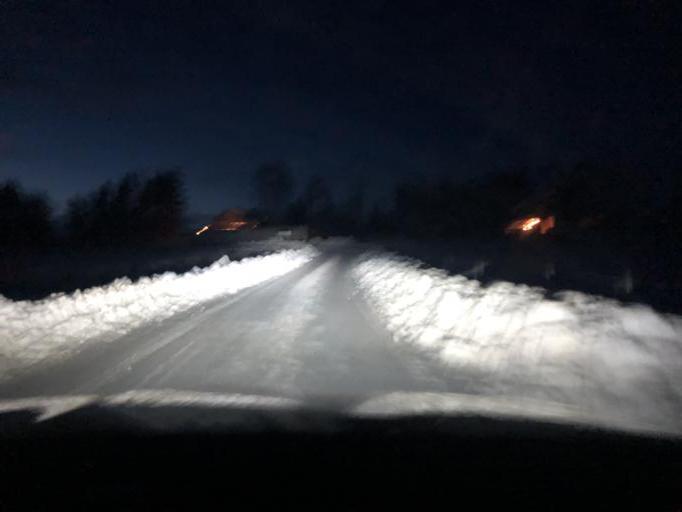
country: SE
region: Vaesternorrland
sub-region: Kramfors Kommun
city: Bollstabruk
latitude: 63.0548
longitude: 17.6483
